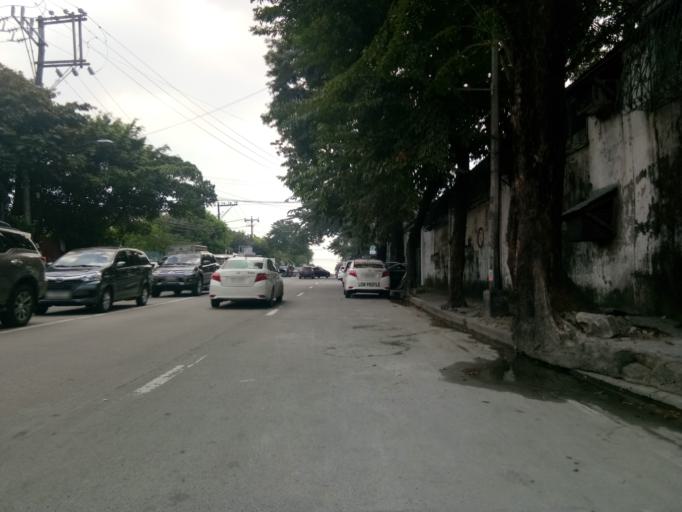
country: PH
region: Metro Manila
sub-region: Marikina
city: Calumpang
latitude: 14.6203
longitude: 121.0632
